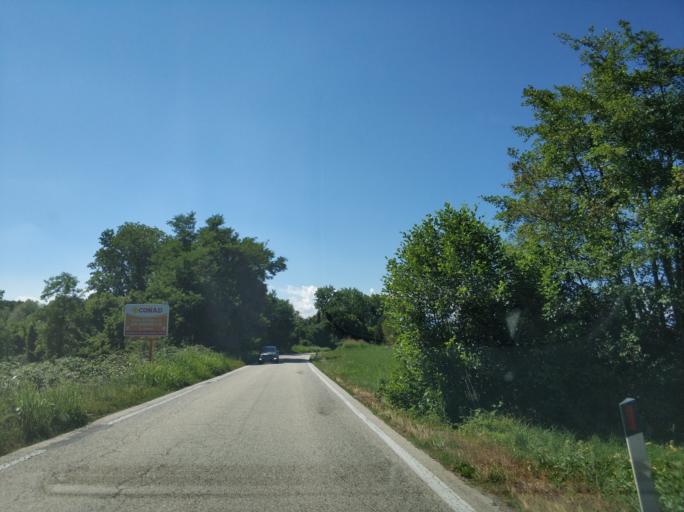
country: IT
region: Piedmont
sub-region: Provincia di Torino
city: San Benigno Canavese
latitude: 45.2174
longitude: 7.7944
